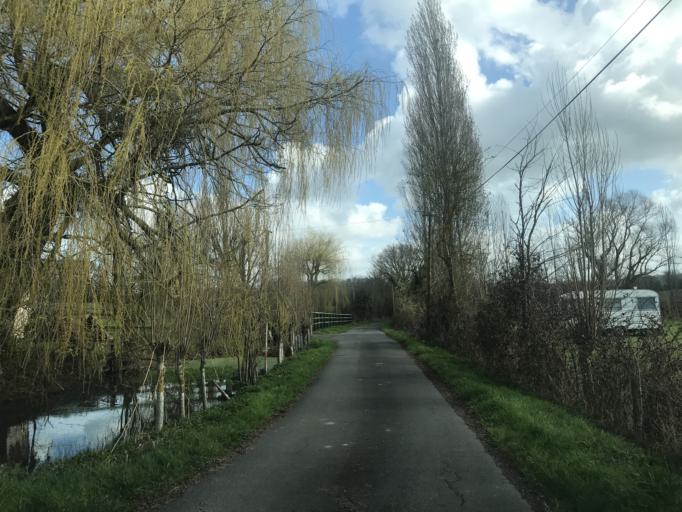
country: FR
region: Lower Normandy
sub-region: Departement du Calvados
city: Dives-sur-Mer
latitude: 49.2671
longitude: -0.1003
